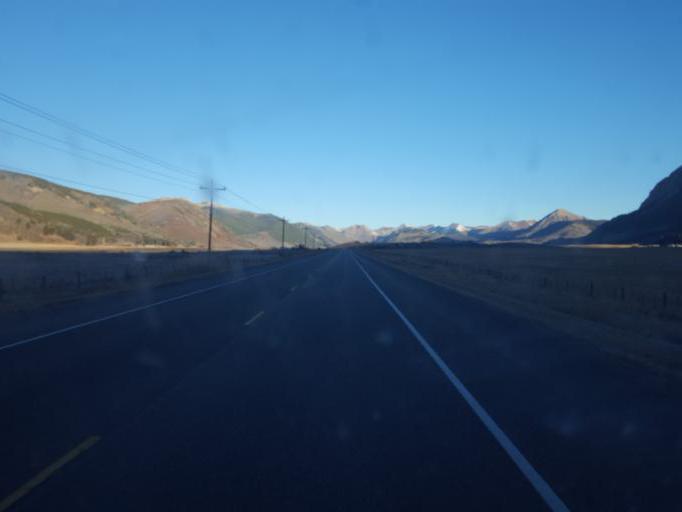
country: US
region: Colorado
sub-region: Gunnison County
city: Crested Butte
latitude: 38.8289
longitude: -106.9233
